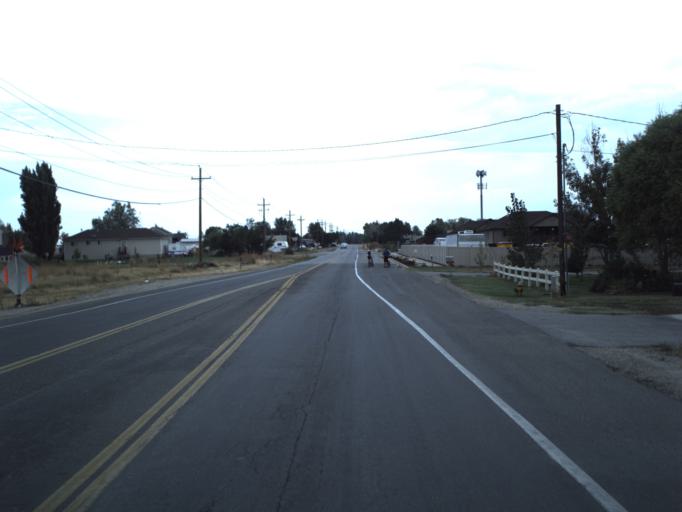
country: US
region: Utah
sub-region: Weber County
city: Hooper
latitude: 41.1919
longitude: -112.0930
